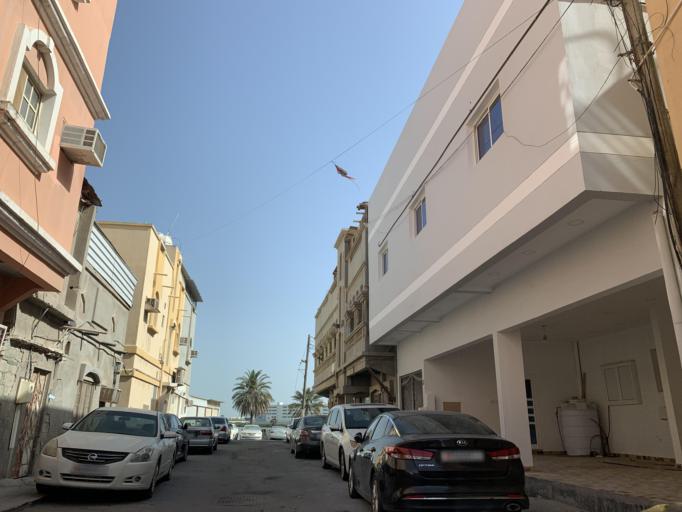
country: BH
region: Northern
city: Sitrah
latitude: 26.1476
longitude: 50.6087
